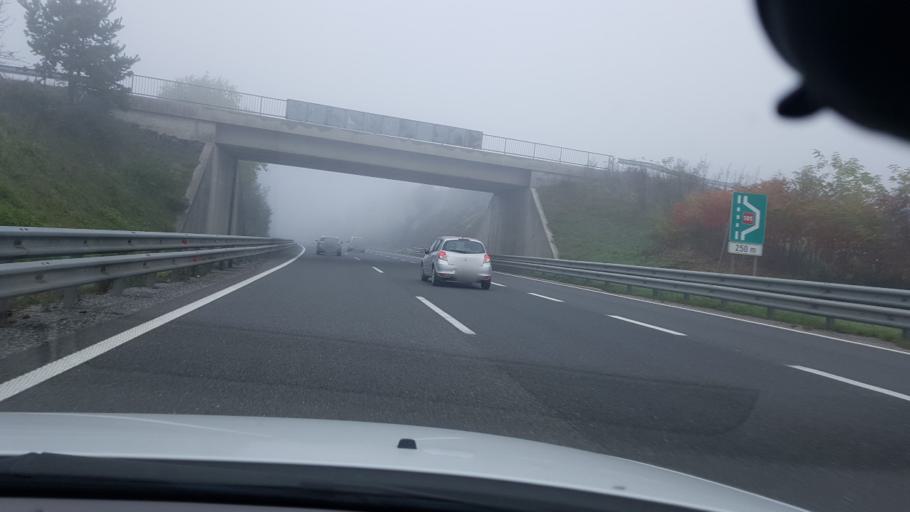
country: SI
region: Grosuplje
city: Grosuplje
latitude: 45.9788
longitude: 14.7000
